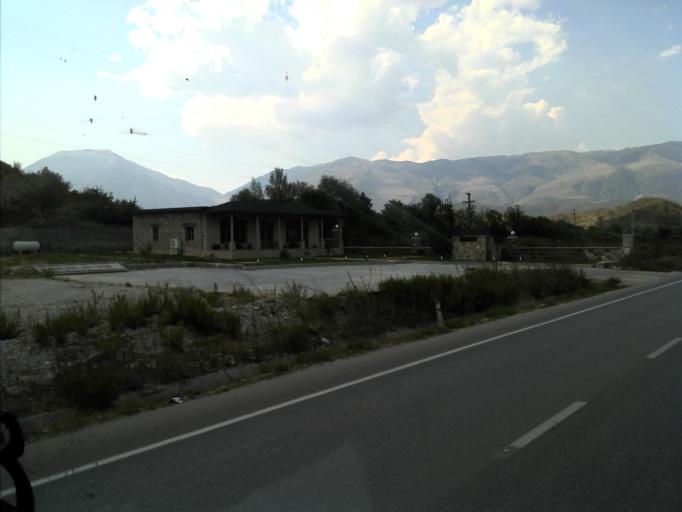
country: AL
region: Gjirokaster
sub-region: Rrethi i Gjirokastres
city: Picar
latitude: 40.1419
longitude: 20.0996
